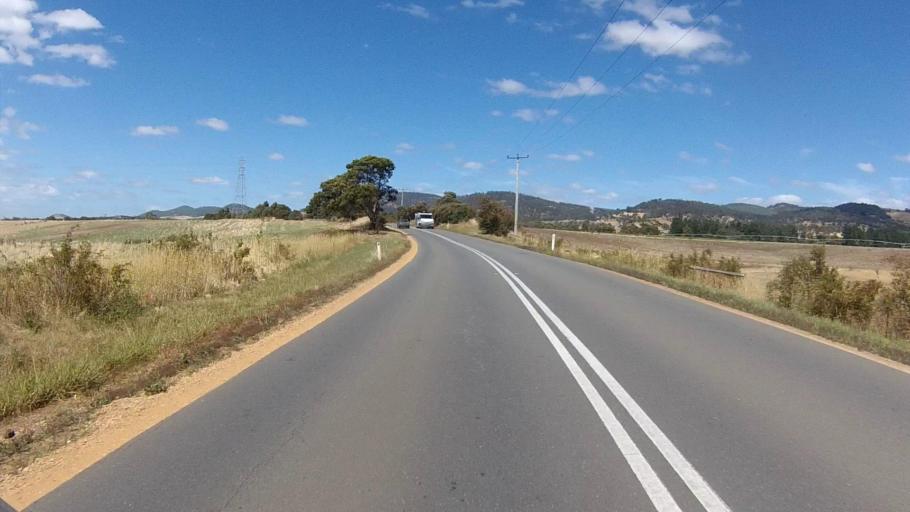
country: AU
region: Tasmania
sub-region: Clarence
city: Cambridge
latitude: -42.7625
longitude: 147.4150
